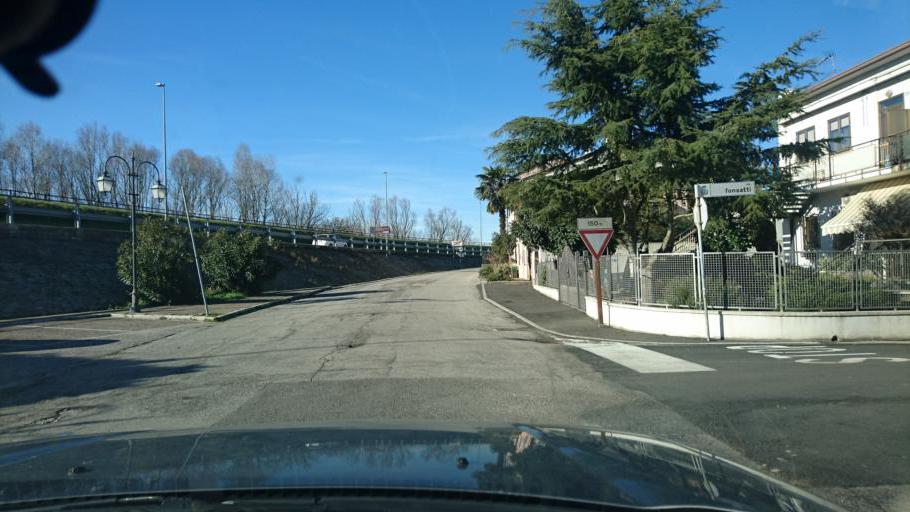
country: IT
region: Veneto
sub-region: Provincia di Rovigo
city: Ariano
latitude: 44.9466
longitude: 12.1188
